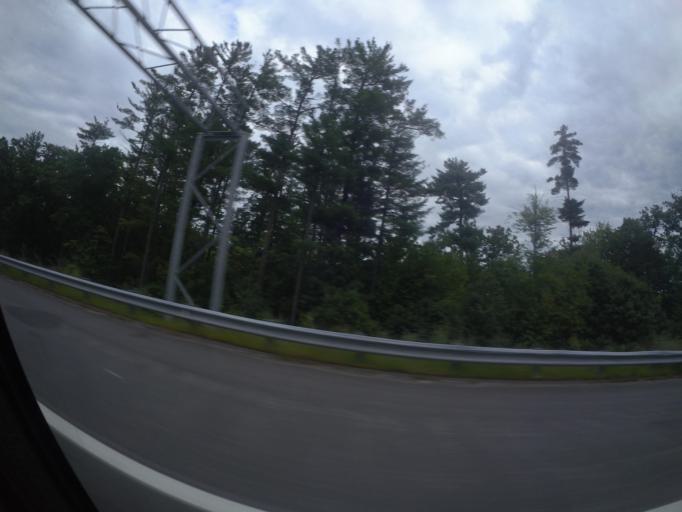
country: US
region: New Hampshire
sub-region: Strafford County
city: Rochester
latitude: 43.3008
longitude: -70.9940
